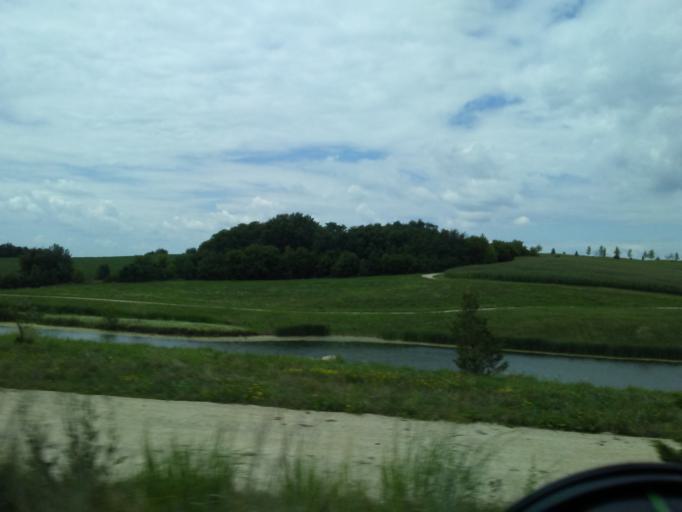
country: US
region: Wisconsin
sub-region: Dane County
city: Verona
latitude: 42.9976
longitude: -89.5702
